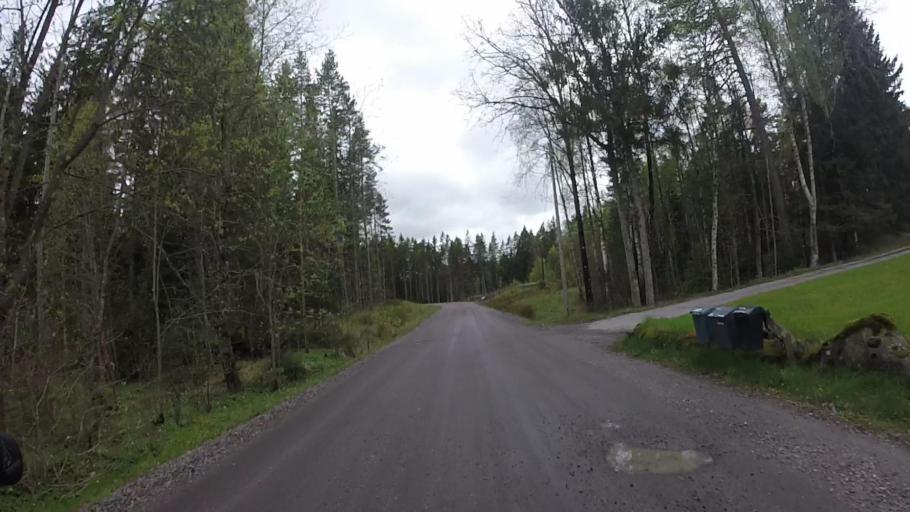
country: SE
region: Vaestra Goetaland
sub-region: Trollhattan
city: Sjuntorp
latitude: 58.2273
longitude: 12.2125
